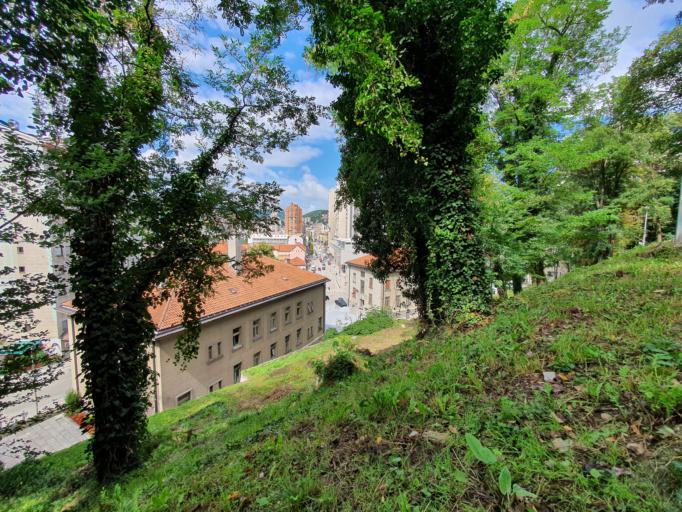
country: RS
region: Central Serbia
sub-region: Zlatiborski Okrug
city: Uzice
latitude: 43.8540
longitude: 19.8468
